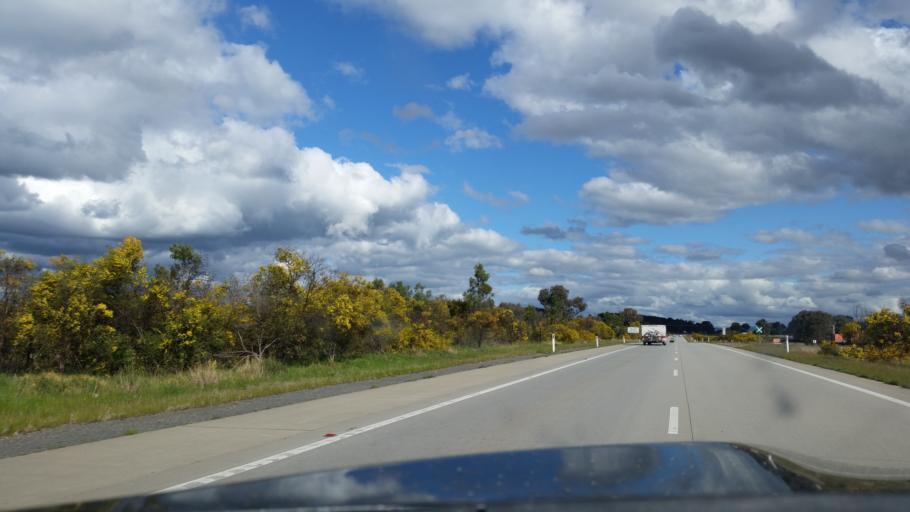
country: AU
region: New South Wales
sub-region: Greater Hume Shire
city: Jindera
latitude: -35.9567
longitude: 147.0046
